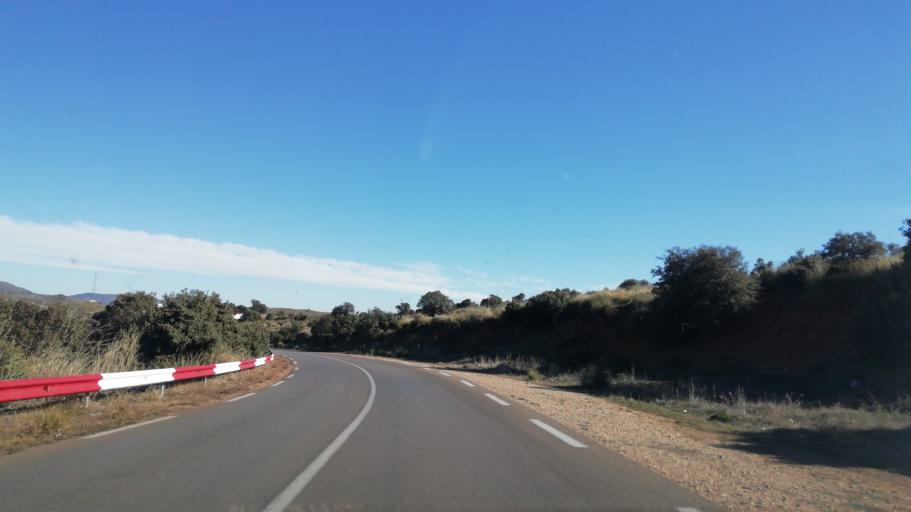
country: DZ
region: Tlemcen
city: Ouled Mimoun
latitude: 34.7580
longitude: -1.1469
